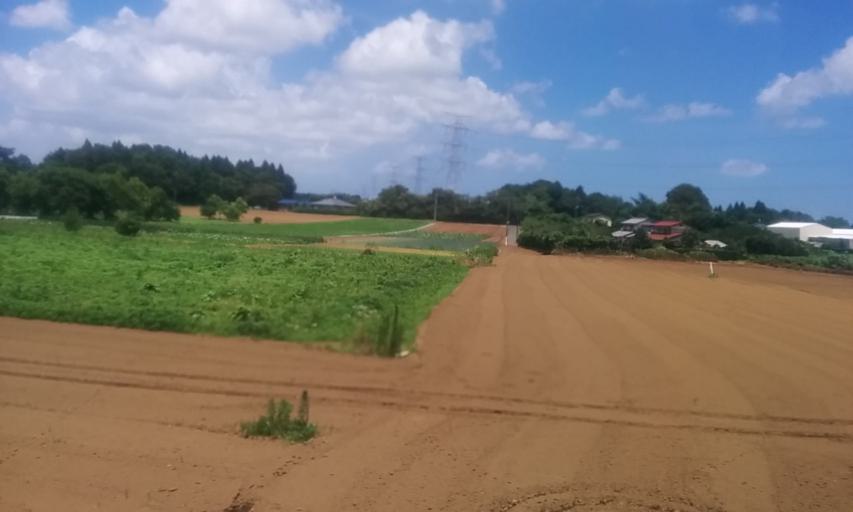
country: JP
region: Chiba
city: Oami
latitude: 35.5383
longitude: 140.2445
